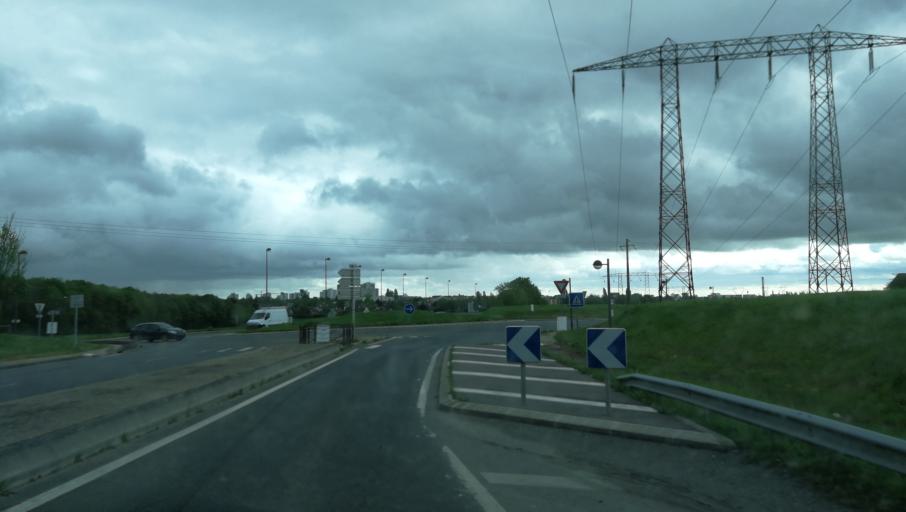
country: FR
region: Ile-de-France
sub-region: Departement de l'Essonne
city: Gometz-le-Chatel
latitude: 48.6724
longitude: 2.1510
